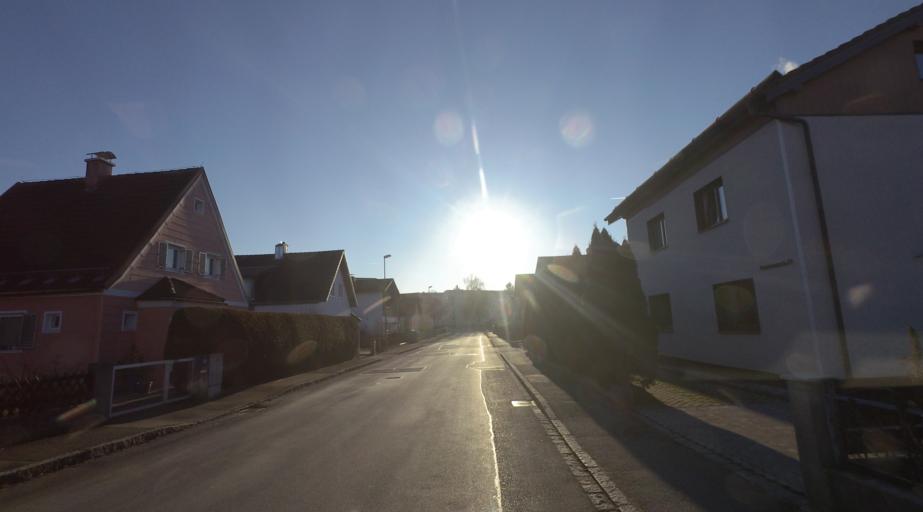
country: DE
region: Bavaria
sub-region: Upper Bavaria
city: Trostberg an der Alz
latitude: 48.0276
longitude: 12.5643
